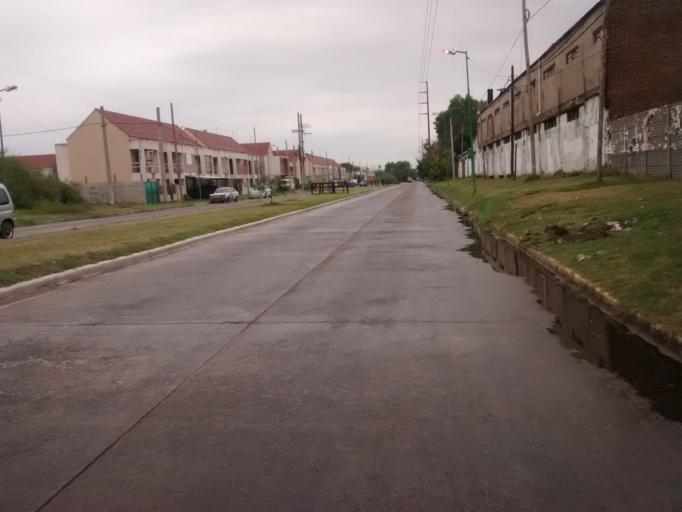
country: AR
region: Buenos Aires
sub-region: Partido de La Plata
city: La Plata
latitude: -34.9066
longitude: -57.9878
